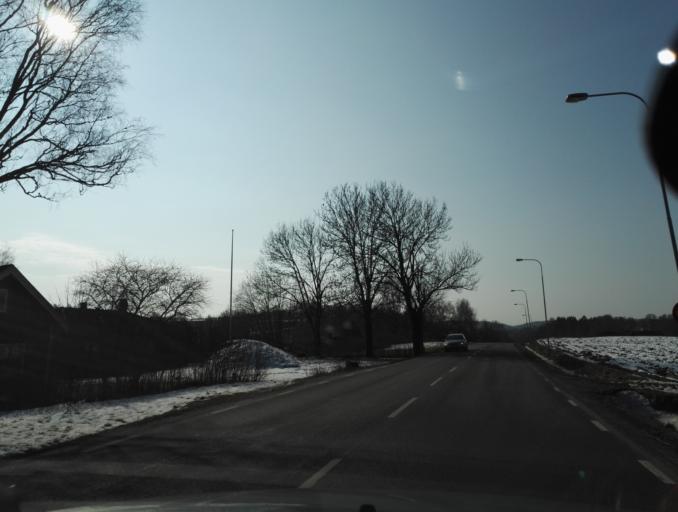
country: SE
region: Vaestra Goetaland
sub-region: Bollebygds Kommun
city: Bollebygd
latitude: 57.6783
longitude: 12.5648
